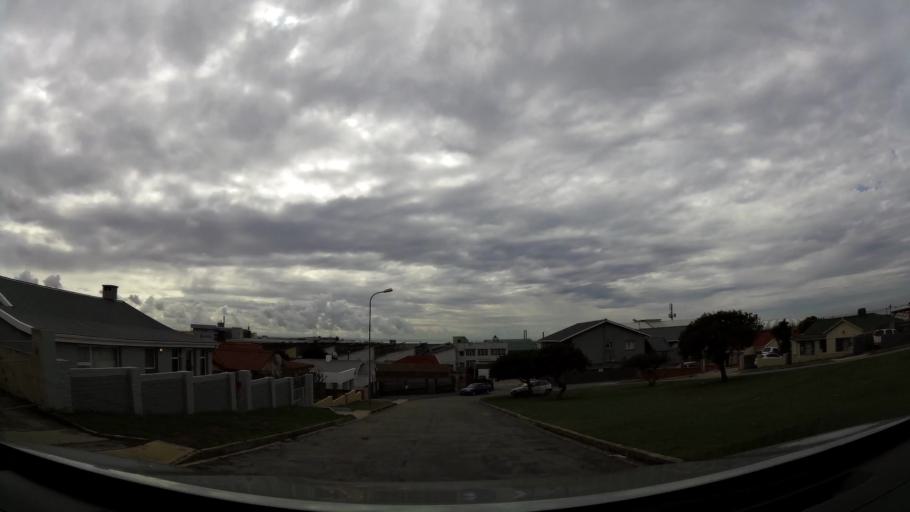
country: ZA
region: Eastern Cape
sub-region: Nelson Mandela Bay Metropolitan Municipality
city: Port Elizabeth
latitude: -33.9393
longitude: 25.5868
